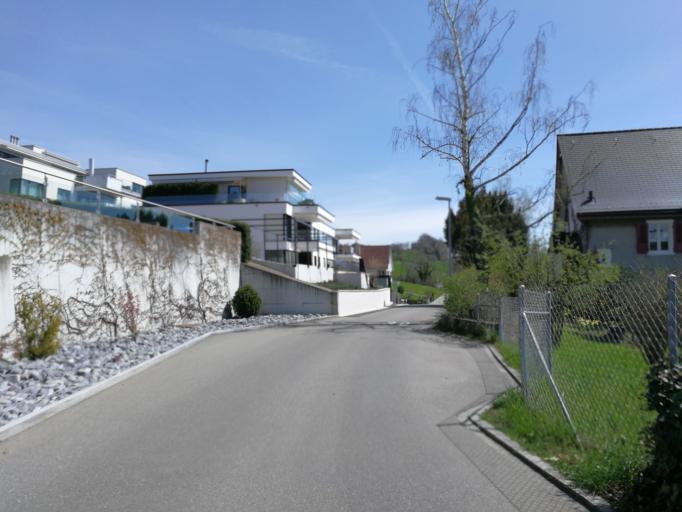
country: CH
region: Zurich
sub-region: Bezirk Meilen
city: Feldmeilen
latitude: 47.2790
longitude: 8.6252
